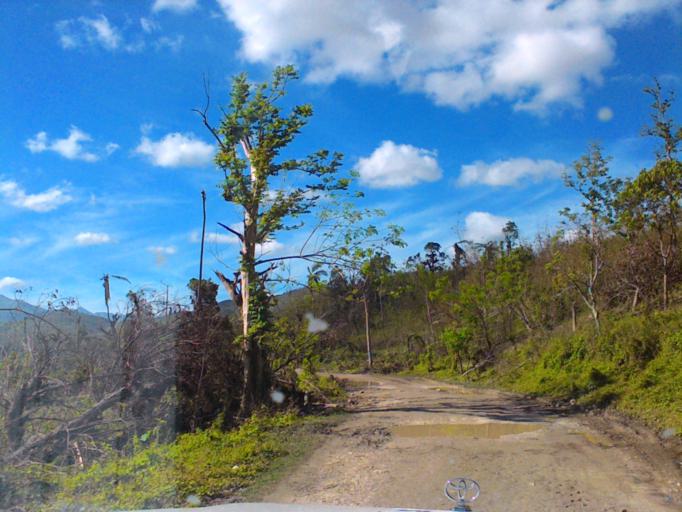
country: HT
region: Grandans
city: Jeremie
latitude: 18.5956
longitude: -74.1058
